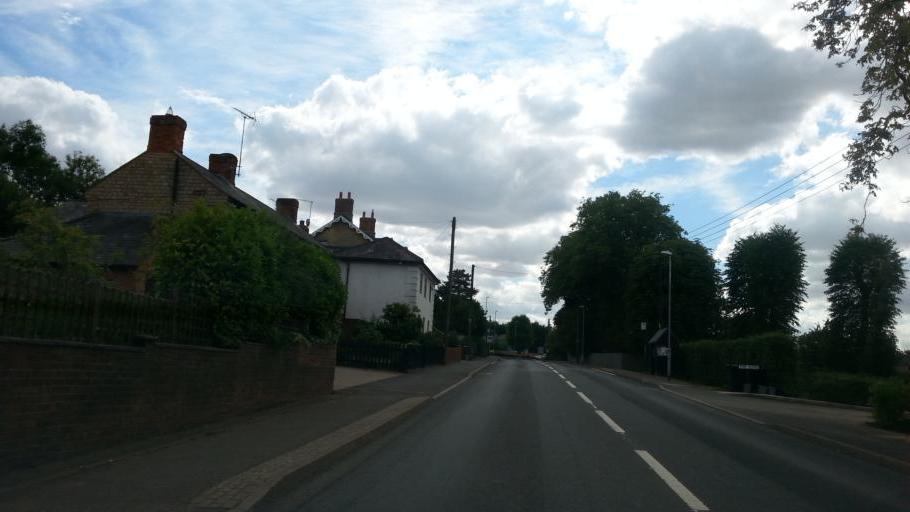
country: GB
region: England
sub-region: Northamptonshire
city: Silverstone
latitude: 52.0846
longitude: -1.0283
